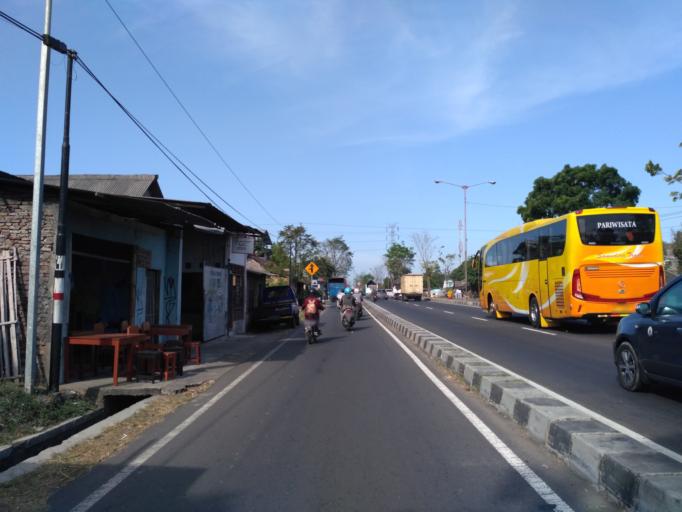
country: ID
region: Daerah Istimewa Yogyakarta
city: Kasihan
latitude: -7.8270
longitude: 110.3486
